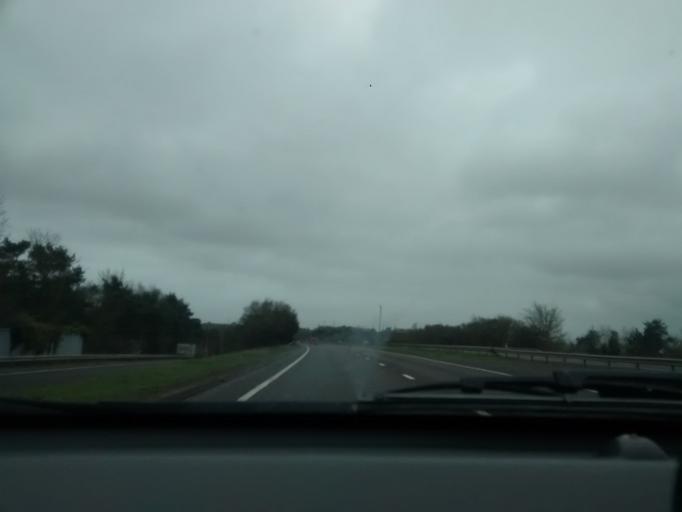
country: GB
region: England
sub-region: Suffolk
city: Bramford
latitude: 52.1064
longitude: 1.1066
